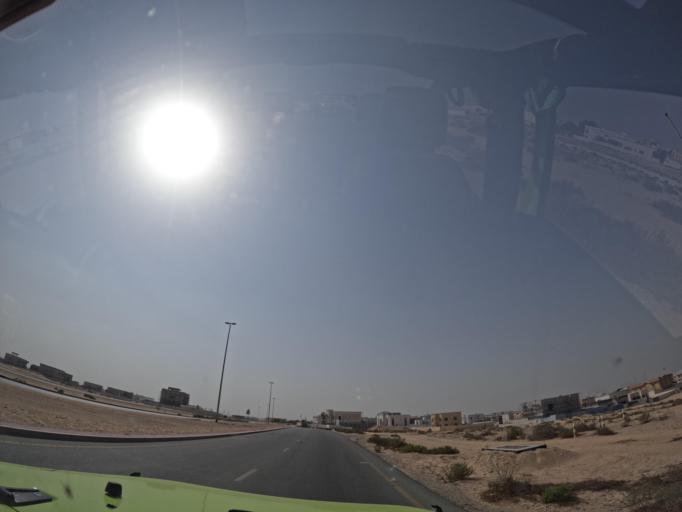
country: AE
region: Ash Shariqah
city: Sharjah
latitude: 25.1967
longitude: 55.4309
